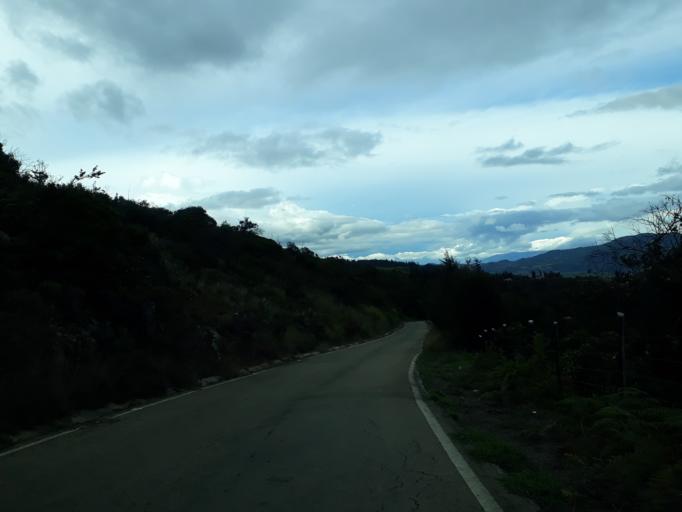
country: CO
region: Cundinamarca
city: Susa
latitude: 5.3989
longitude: -73.7798
